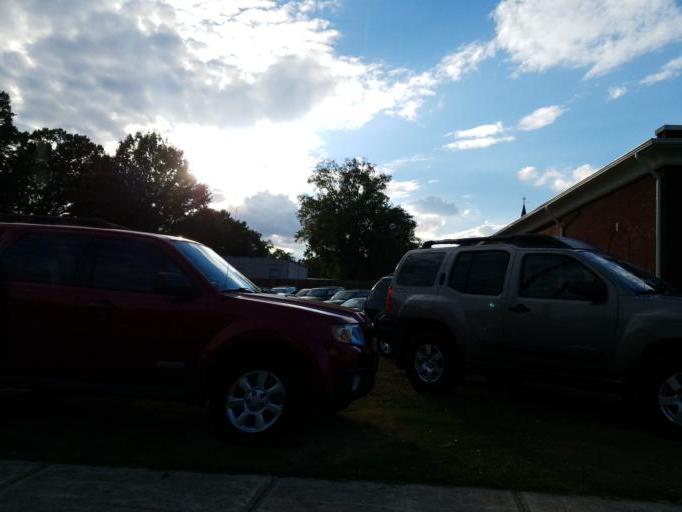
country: US
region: Georgia
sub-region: Bartow County
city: Cartersville
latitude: 34.1756
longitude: -84.7935
